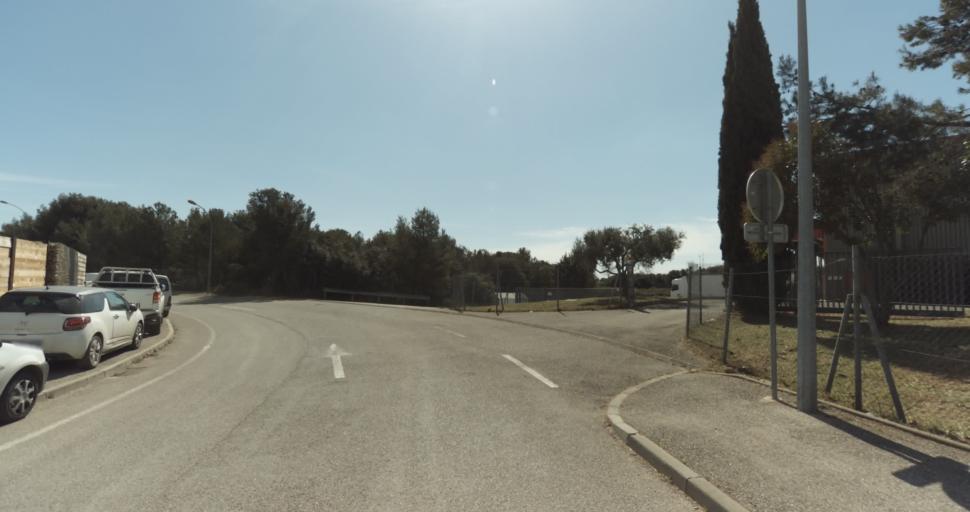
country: FR
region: Provence-Alpes-Cote d'Azur
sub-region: Departement des Bouches-du-Rhone
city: Lambesc
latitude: 43.6474
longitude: 5.2546
